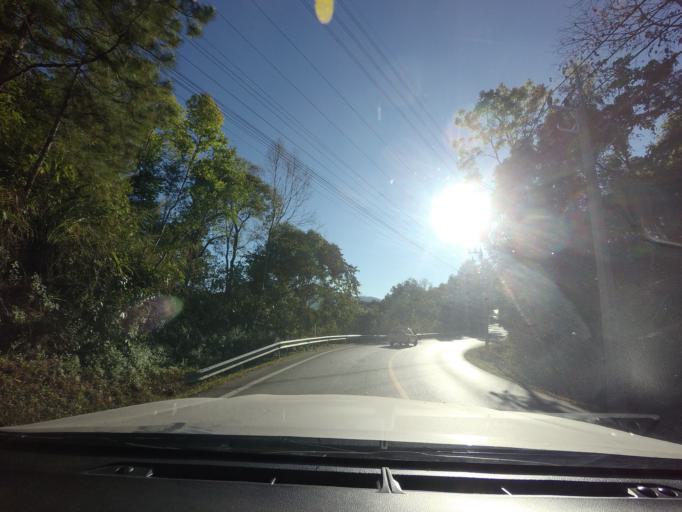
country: TH
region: Mae Hong Son
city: Mae Hi
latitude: 19.2712
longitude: 98.5975
